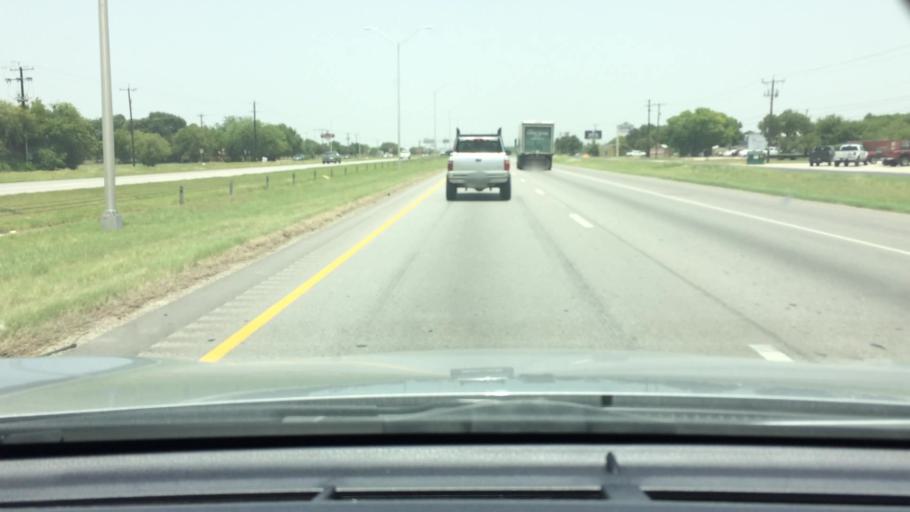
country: US
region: Texas
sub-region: Bexar County
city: China Grove
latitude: 29.4045
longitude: -98.3893
